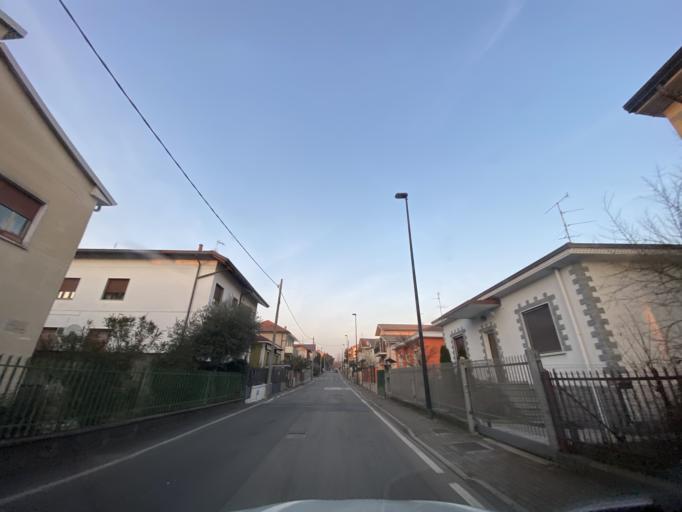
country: IT
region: Lombardy
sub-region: Provincia di Monza e Brianza
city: Villaggio del Sole
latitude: 45.6135
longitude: 9.1063
